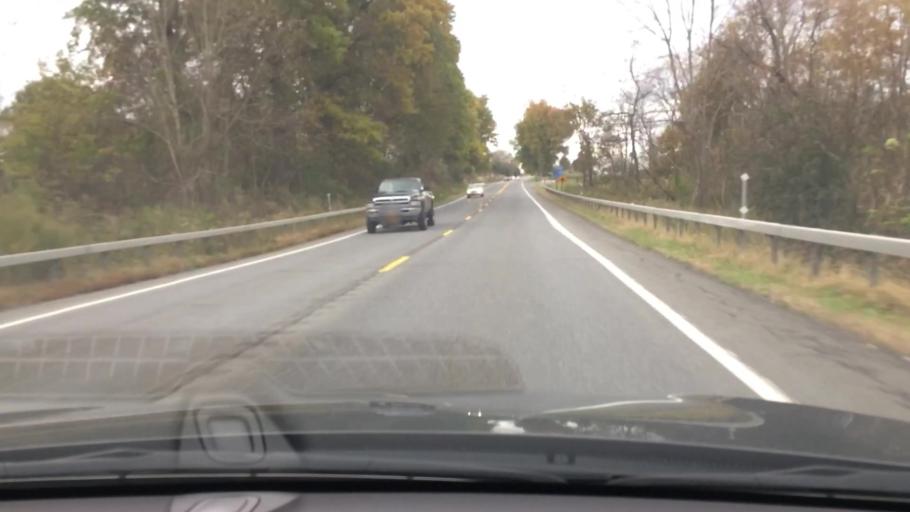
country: US
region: New York
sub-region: Columbia County
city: Stottville
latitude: 42.3208
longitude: -73.7025
